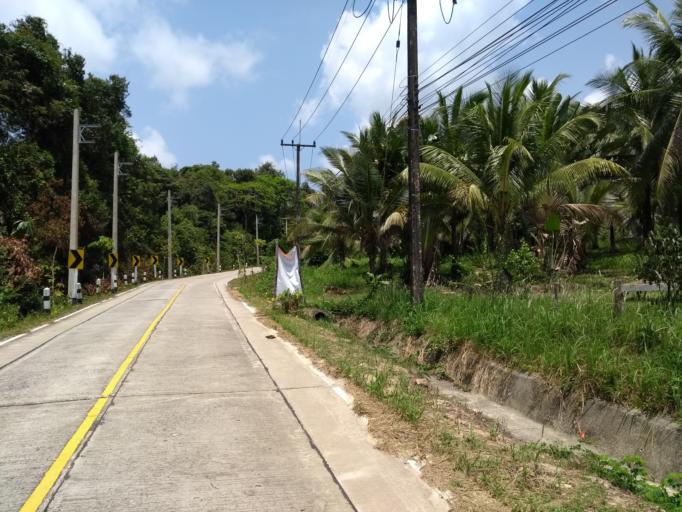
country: TH
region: Trat
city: Ko Kut
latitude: 11.6103
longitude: 102.5515
